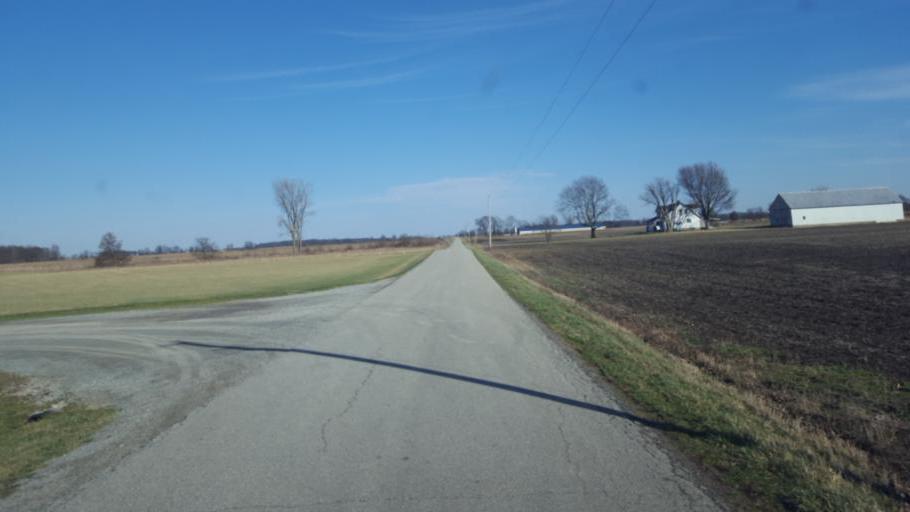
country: US
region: Ohio
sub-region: Crawford County
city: Bucyrus
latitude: 40.7031
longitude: -83.0359
